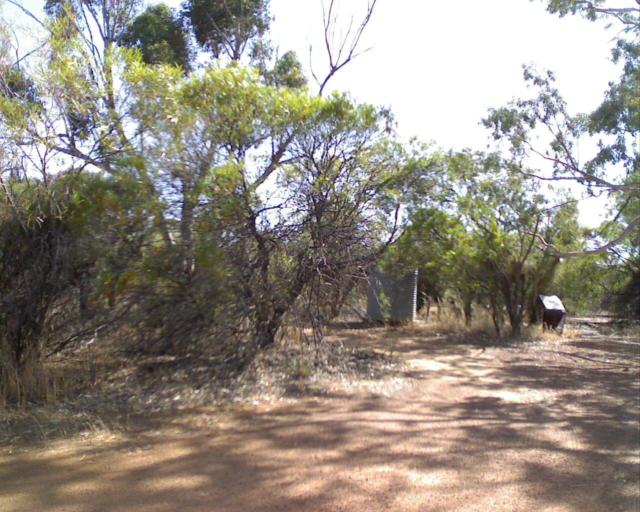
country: AU
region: Western Australia
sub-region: Moora
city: Moora
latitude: -29.8645
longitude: 116.1658
